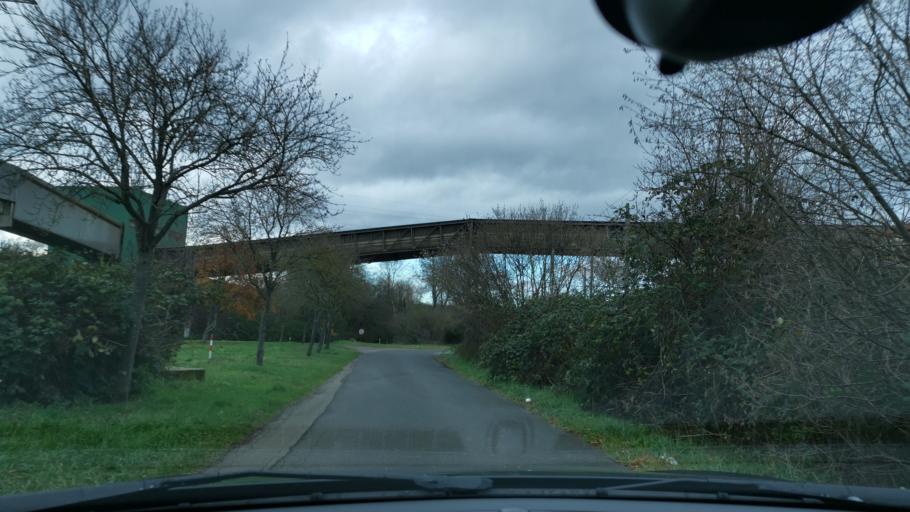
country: DE
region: North Rhine-Westphalia
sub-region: Regierungsbezirk Dusseldorf
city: Grevenbroich
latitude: 51.0510
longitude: 6.5707
